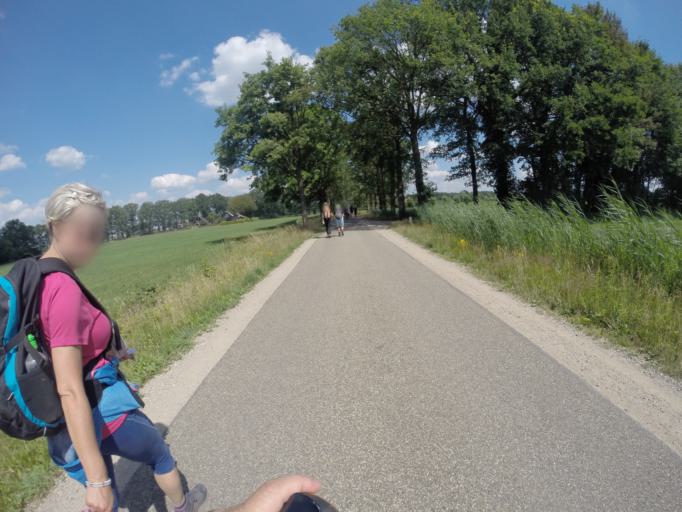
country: NL
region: Gelderland
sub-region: Gemeente Lochem
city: Barchem
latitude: 52.1170
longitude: 6.4349
